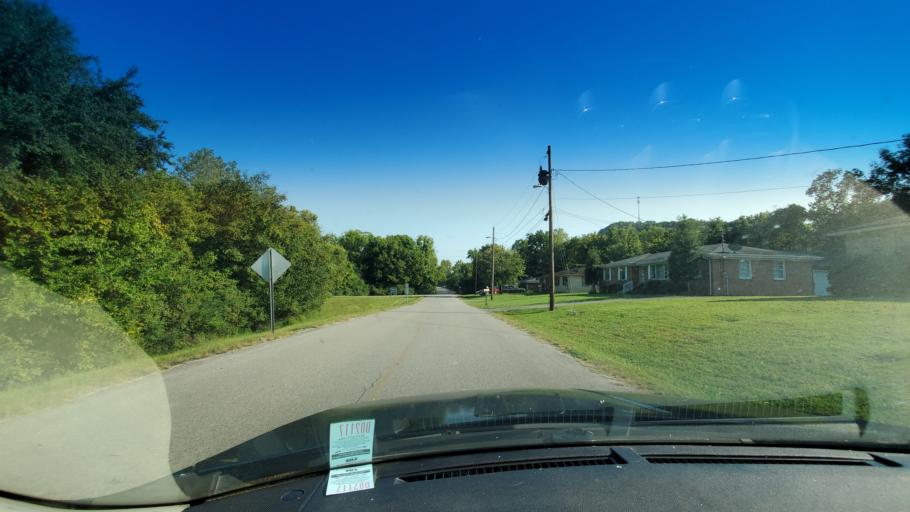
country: US
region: Tennessee
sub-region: Smith County
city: Carthage
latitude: 36.2550
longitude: -85.9571
